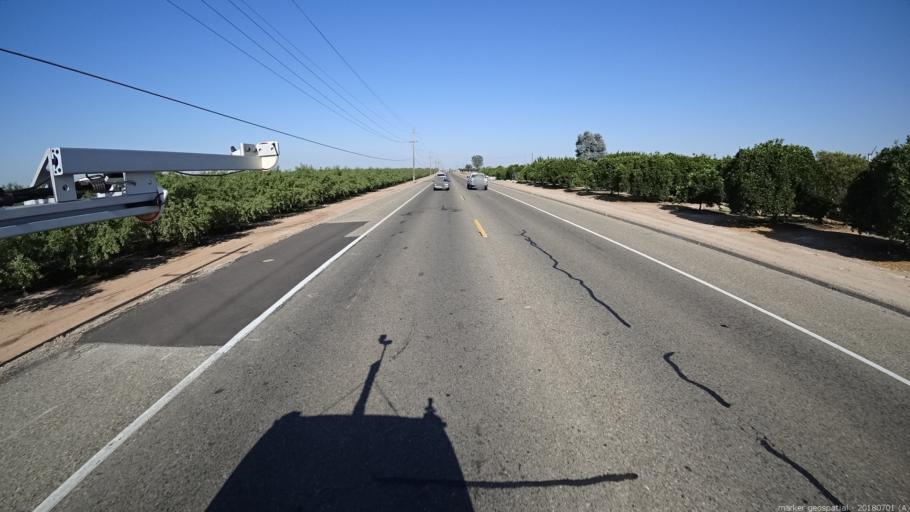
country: US
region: California
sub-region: Madera County
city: Bonadelle Ranchos-Madera Ranchos
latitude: 36.9231
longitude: -119.8263
